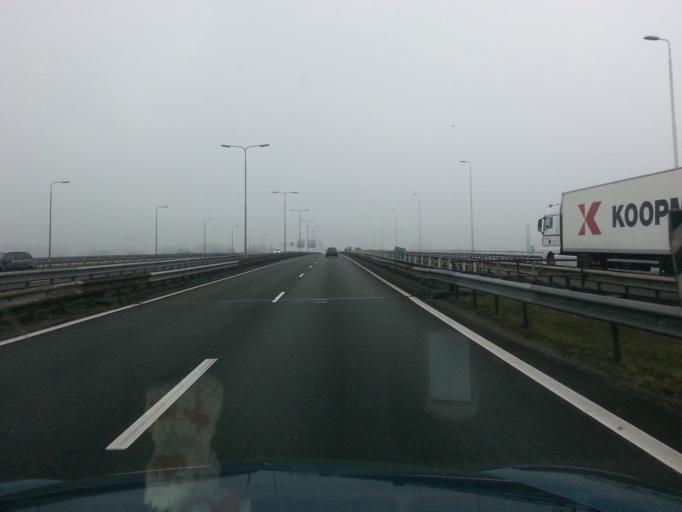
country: NL
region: Gelderland
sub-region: Gemeente Rheden
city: Velp
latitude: 51.9771
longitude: 5.9865
